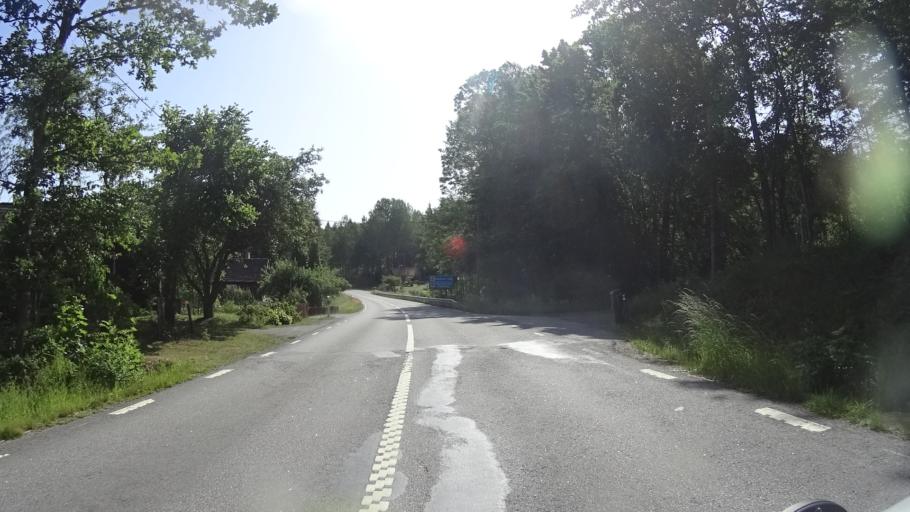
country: SE
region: Kalmar
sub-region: Vasterviks Kommun
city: Overum
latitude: 58.0783
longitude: 16.1683
